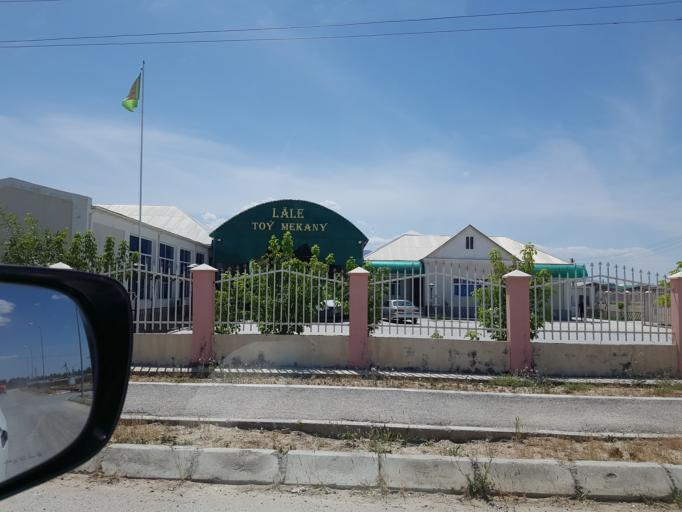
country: TM
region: Ahal
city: Abadan
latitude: 38.1726
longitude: 57.9581
